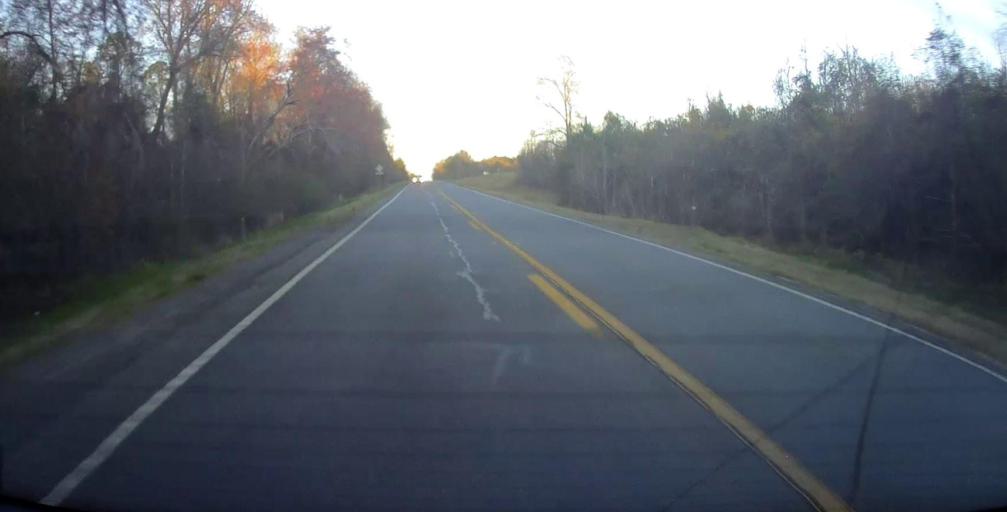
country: US
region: Georgia
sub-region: Dodge County
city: Eastman
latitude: 32.2749
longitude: -83.1156
